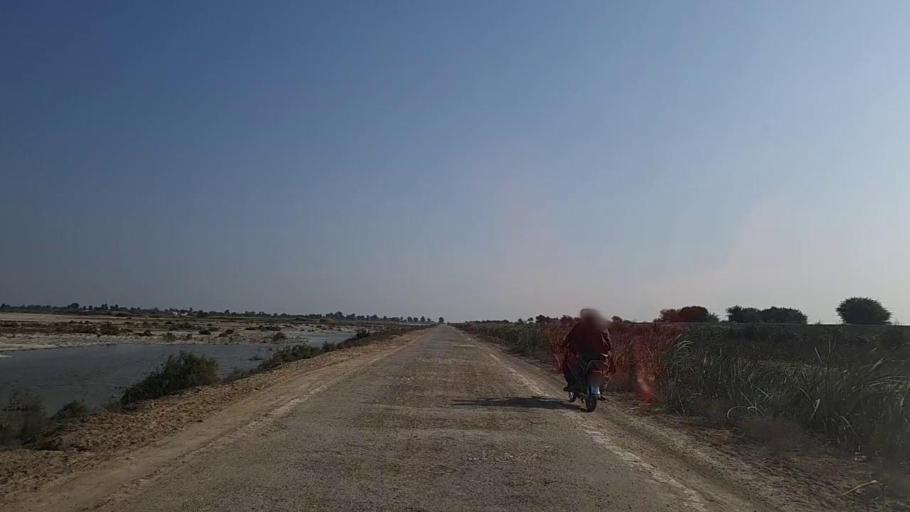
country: PK
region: Sindh
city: Sanghar
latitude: 25.9790
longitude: 69.0250
